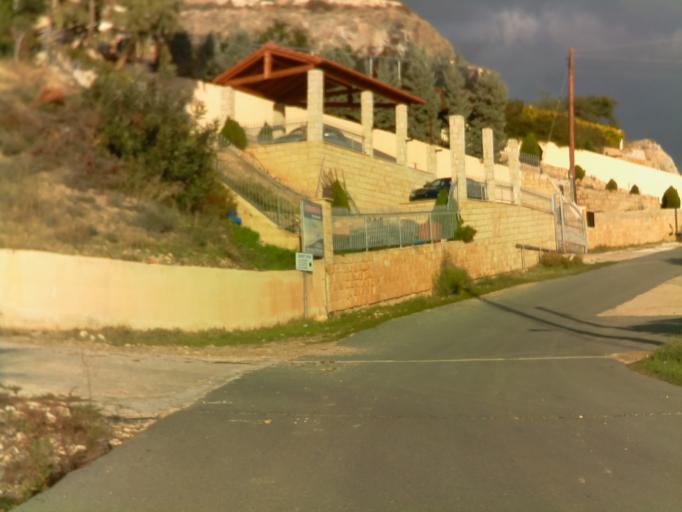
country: CY
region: Pafos
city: Kissonerga
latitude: 34.8496
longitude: 32.3928
